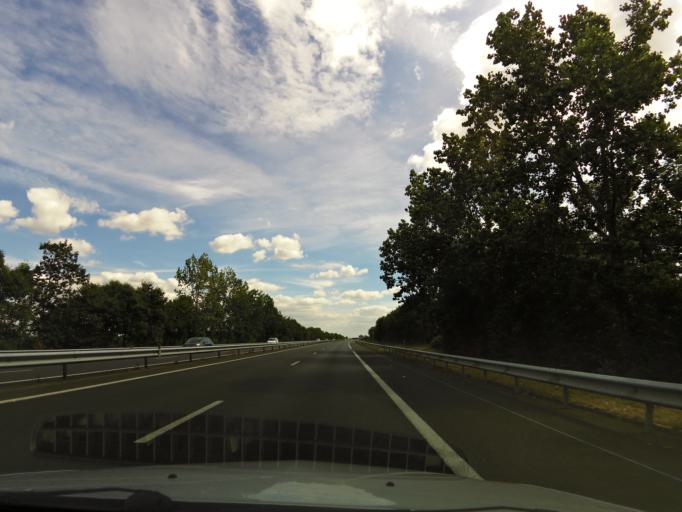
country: FR
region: Pays de la Loire
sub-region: Departement de la Vendee
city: Les Brouzils
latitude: 46.8951
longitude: -1.2999
